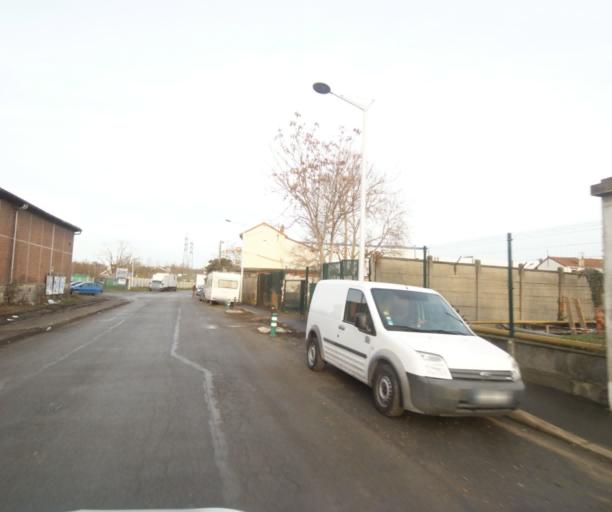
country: FR
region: Ile-de-France
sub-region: Departement des Yvelines
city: Carrieres-sur-Seine
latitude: 48.8994
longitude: 2.1826
